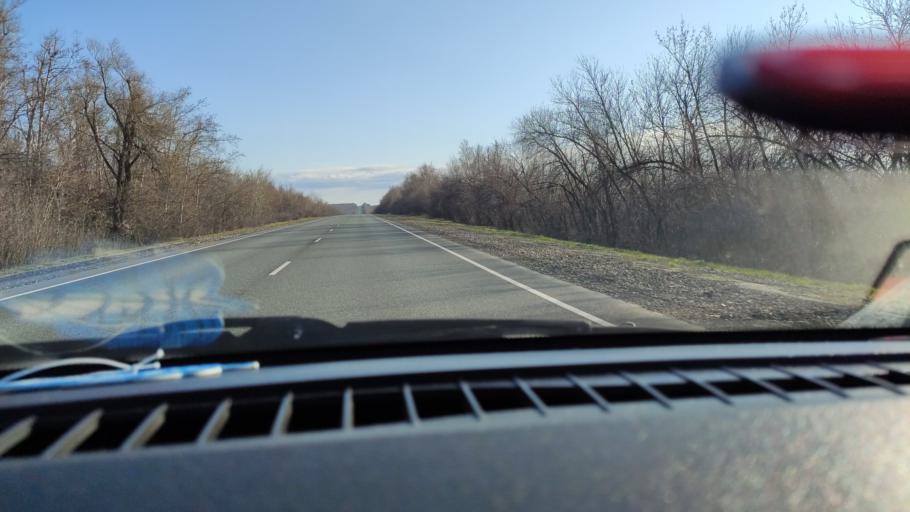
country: RU
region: Saratov
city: Khvalynsk
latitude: 52.5998
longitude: 48.1431
